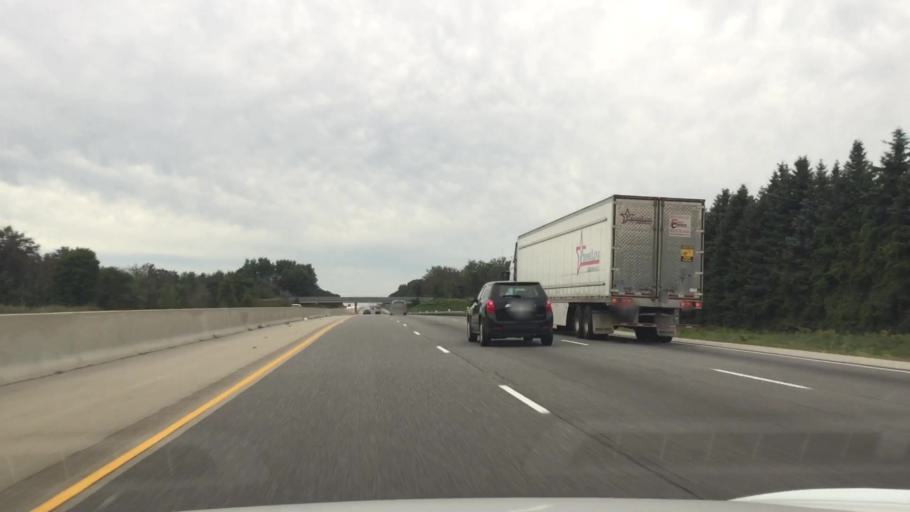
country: CA
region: Ontario
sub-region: Oxford County
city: Woodstock
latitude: 43.1689
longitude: -80.6607
